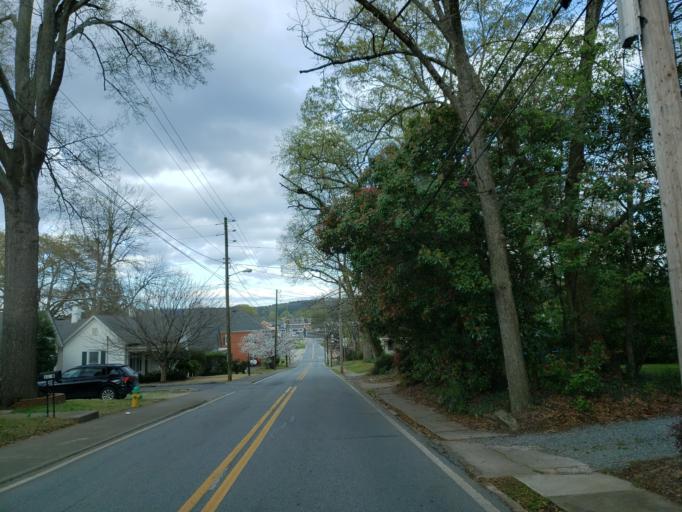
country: US
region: Georgia
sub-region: Bartow County
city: Cartersville
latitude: 34.1631
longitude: -84.7977
